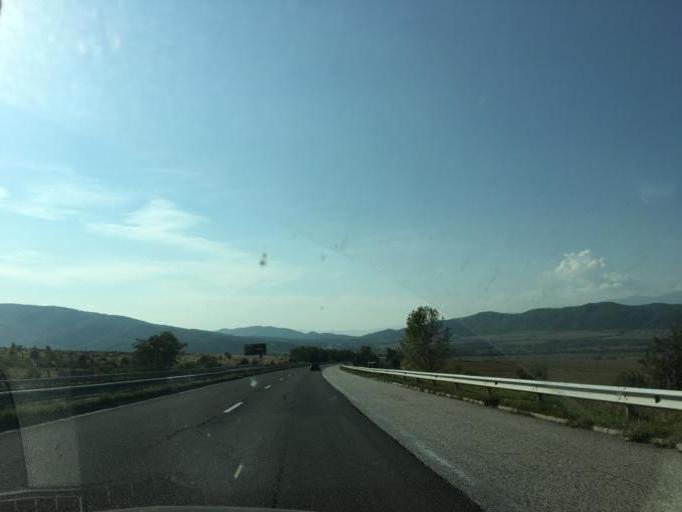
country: BG
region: Sofiya
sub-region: Obshtina Ikhtiman
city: Ikhtiman
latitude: 42.4213
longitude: 23.8575
